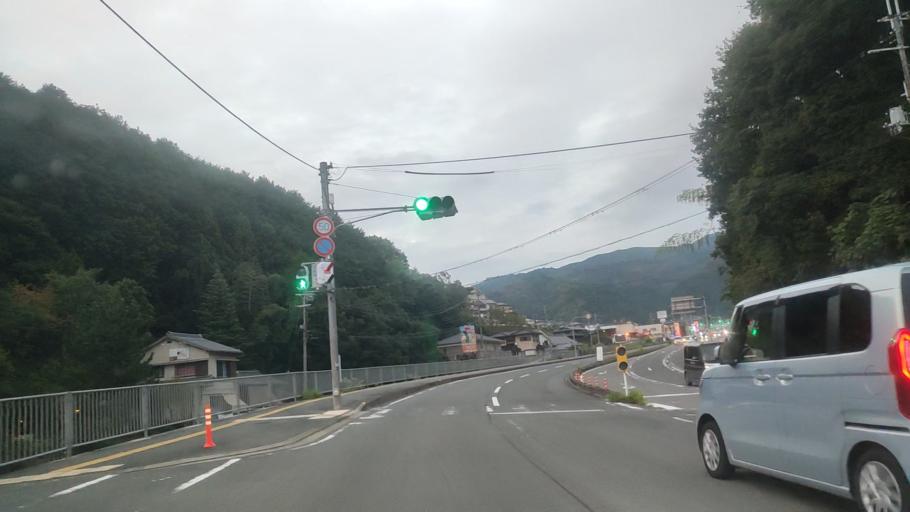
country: JP
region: Wakayama
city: Hashimoto
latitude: 34.3629
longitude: 135.6056
